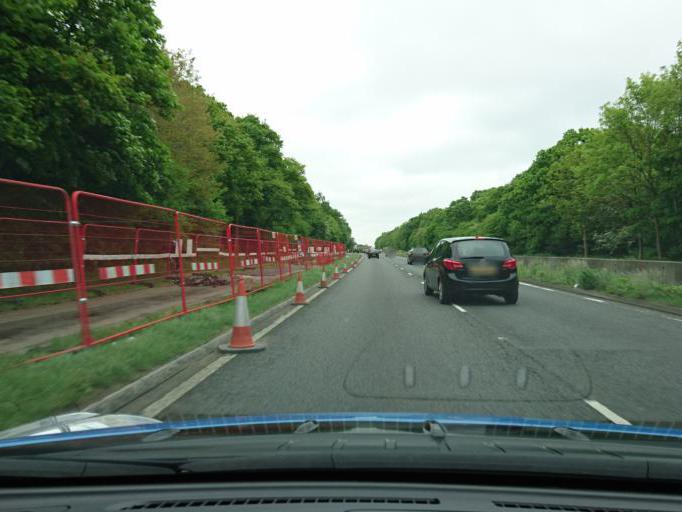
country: GB
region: England
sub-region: Oxfordshire
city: Cowley
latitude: 51.7469
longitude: -1.1955
